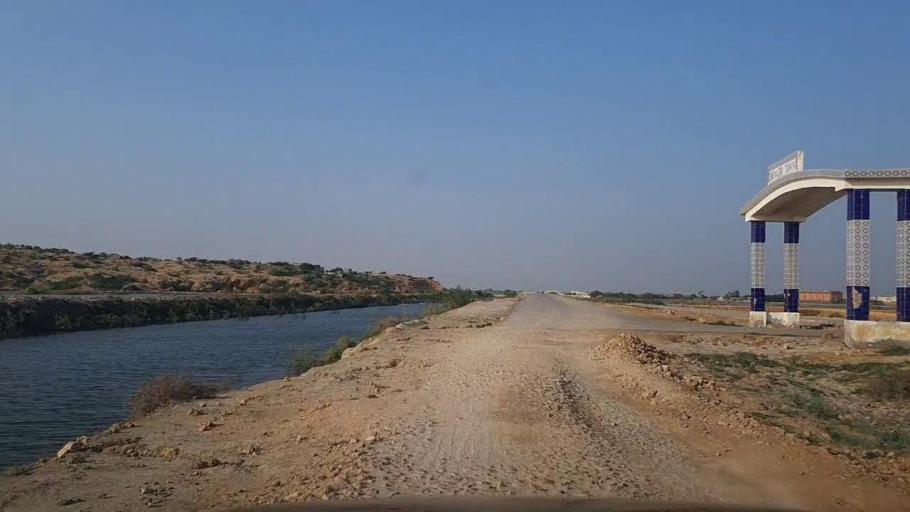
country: PK
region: Sindh
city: Thatta
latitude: 24.7408
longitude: 67.9066
